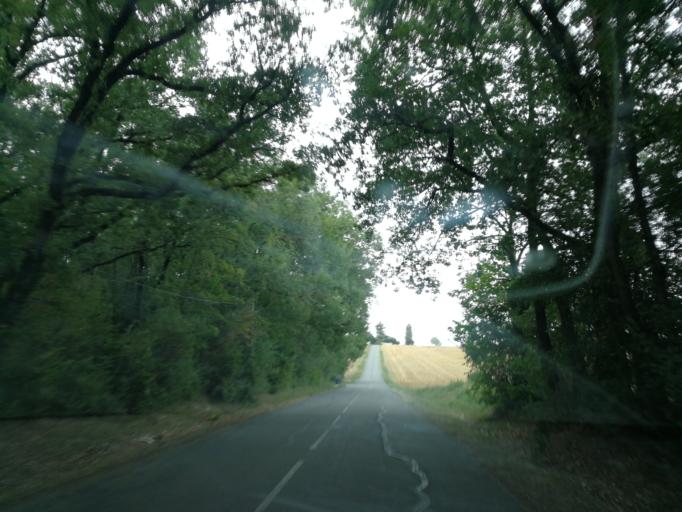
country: FR
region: Midi-Pyrenees
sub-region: Departement de la Haute-Garonne
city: Flourens
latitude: 43.6058
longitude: 1.5369
